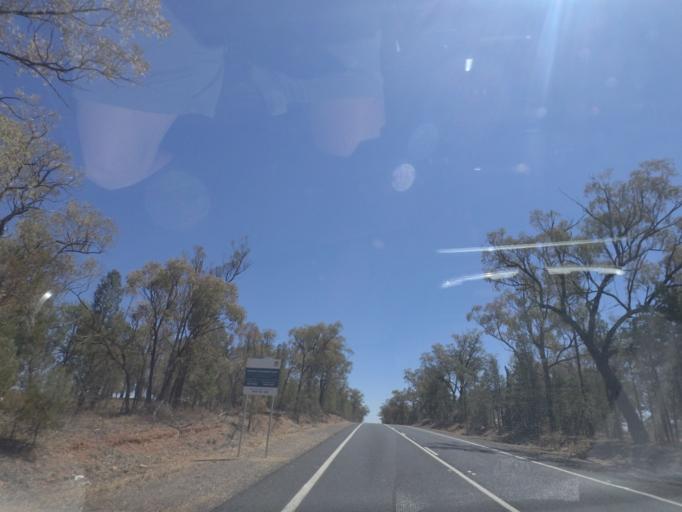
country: AU
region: New South Wales
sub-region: Gilgandra
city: Gilgandra
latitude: -31.4851
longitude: 148.8809
